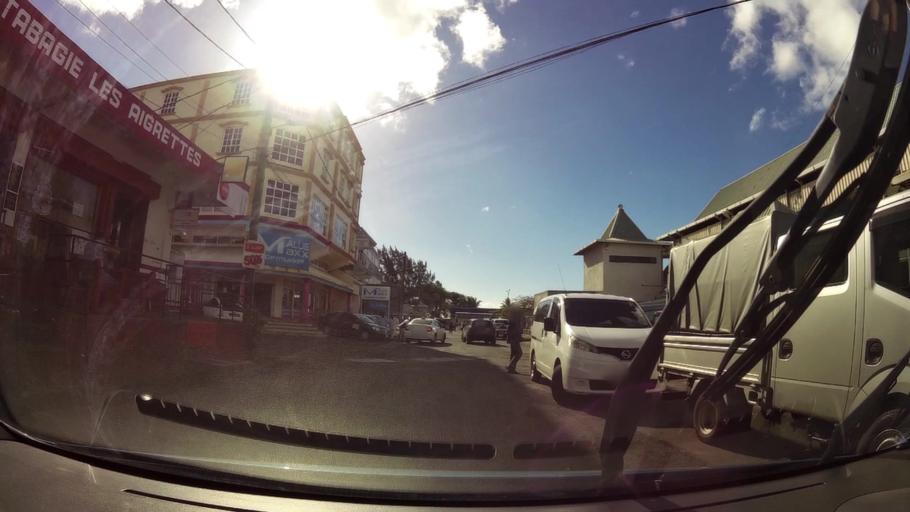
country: MU
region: Grand Port
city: Mahebourg
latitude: -20.4068
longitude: 57.7077
